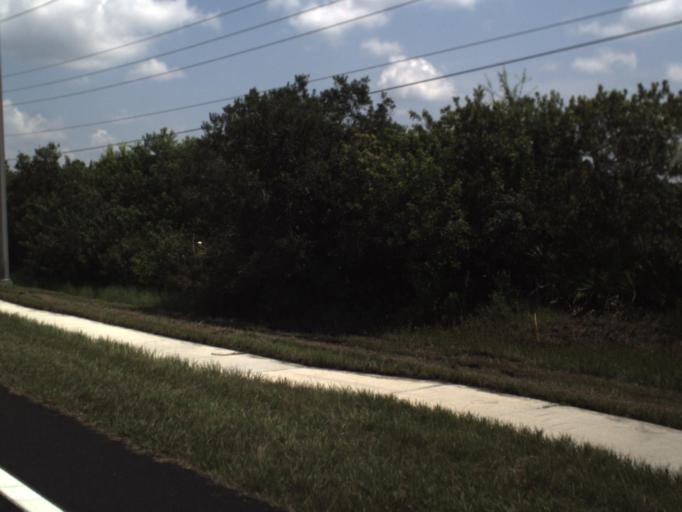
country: US
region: Florida
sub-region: Hillsborough County
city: Cheval
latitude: 28.1316
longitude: -82.5023
